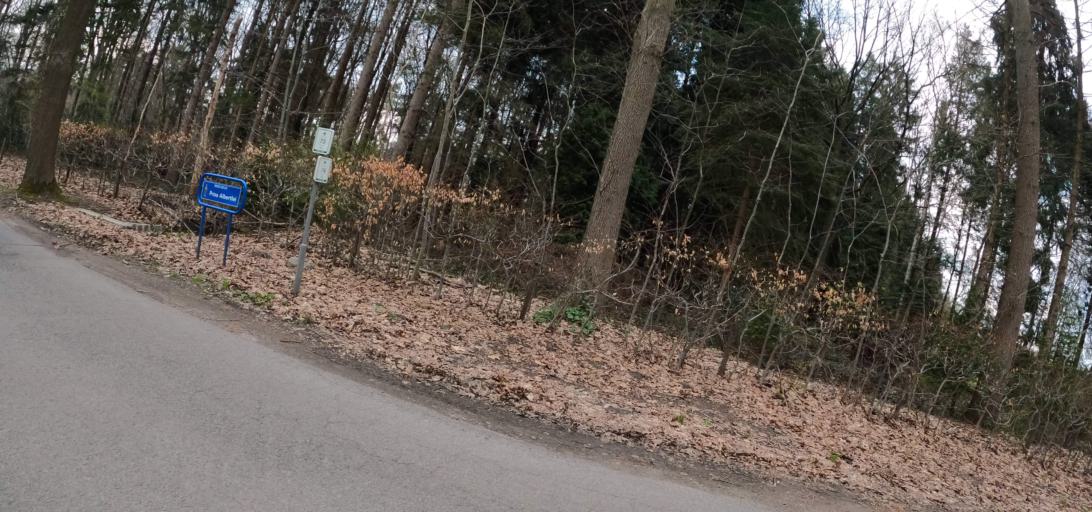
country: BE
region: Flanders
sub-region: Provincie Antwerpen
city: Kalmthout
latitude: 51.3545
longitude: 4.4688
